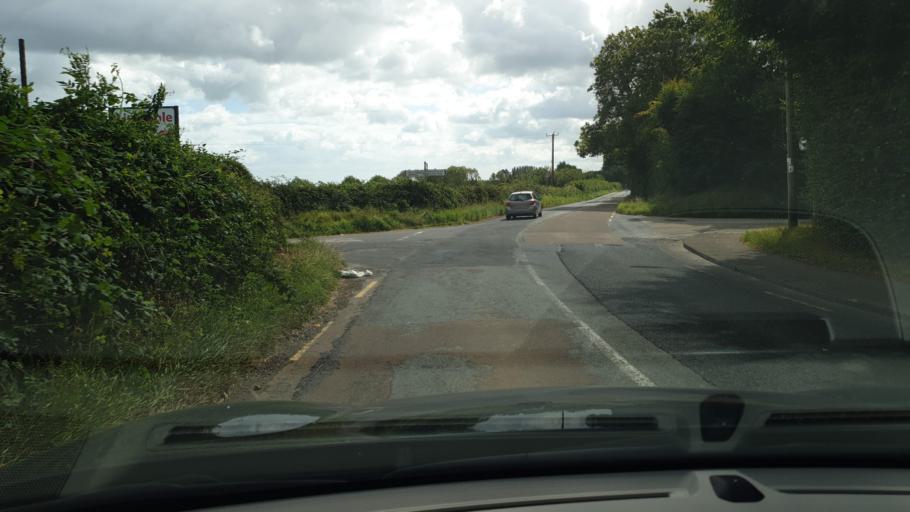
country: IE
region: Leinster
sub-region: Fingal County
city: Swords
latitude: 53.4824
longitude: -6.2858
